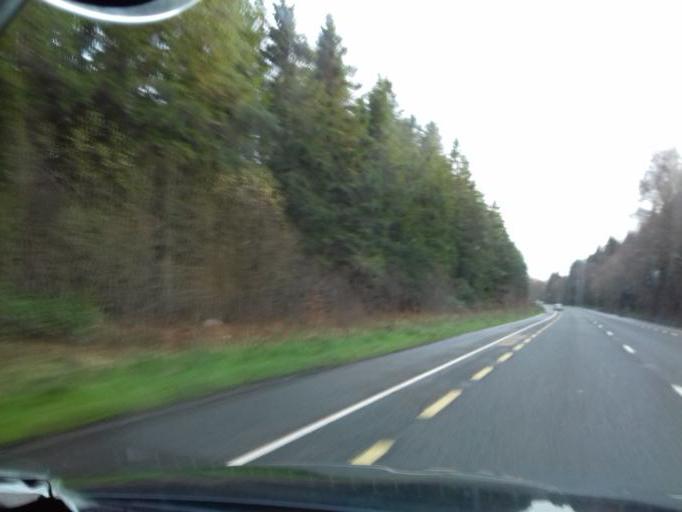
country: IE
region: Leinster
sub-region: Laois
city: Abbeyleix
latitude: 52.8869
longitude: -7.3645
